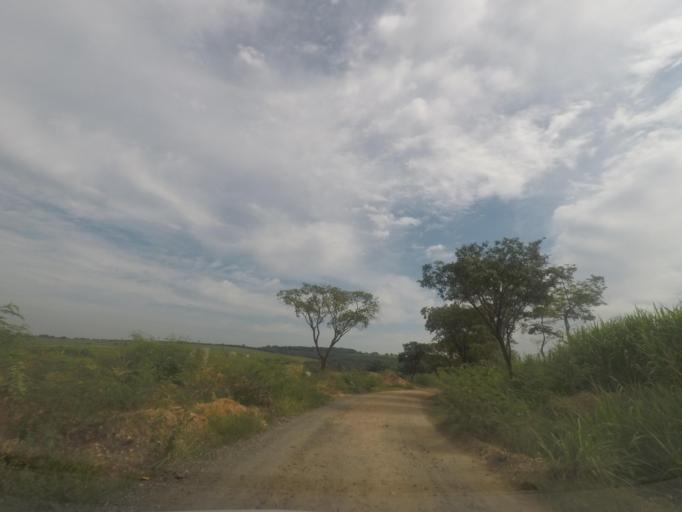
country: BR
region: Sao Paulo
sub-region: Sumare
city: Sumare
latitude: -22.8014
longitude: -47.2563
